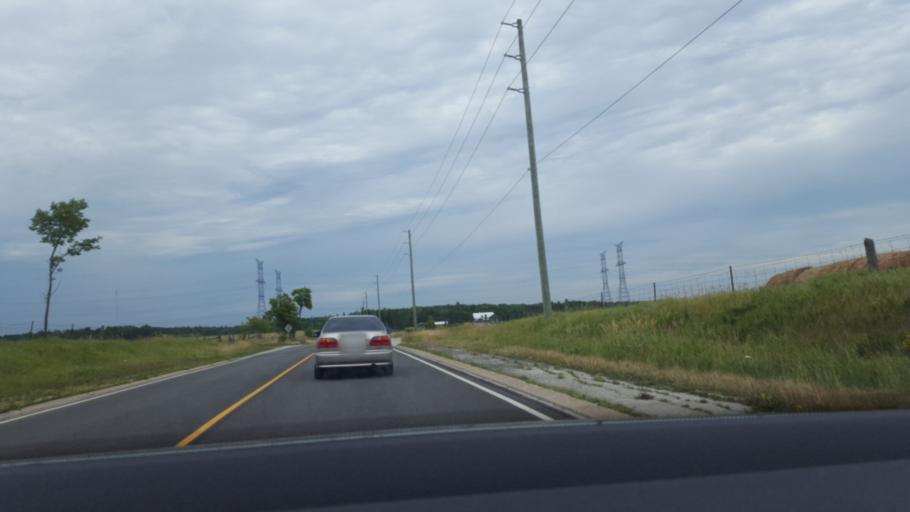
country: CA
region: Ontario
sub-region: Halton
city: Milton
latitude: 43.5603
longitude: -79.8991
